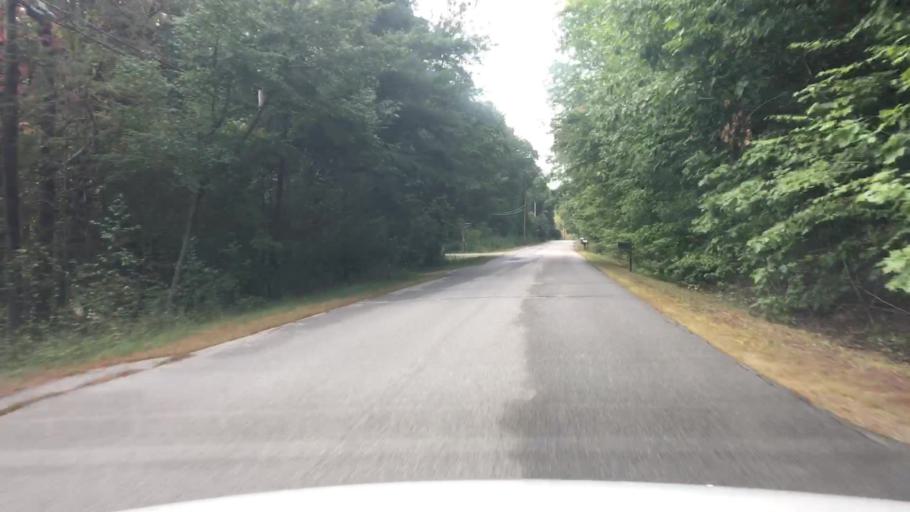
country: US
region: Maine
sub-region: York County
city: Kittery Point
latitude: 43.1081
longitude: -70.6923
